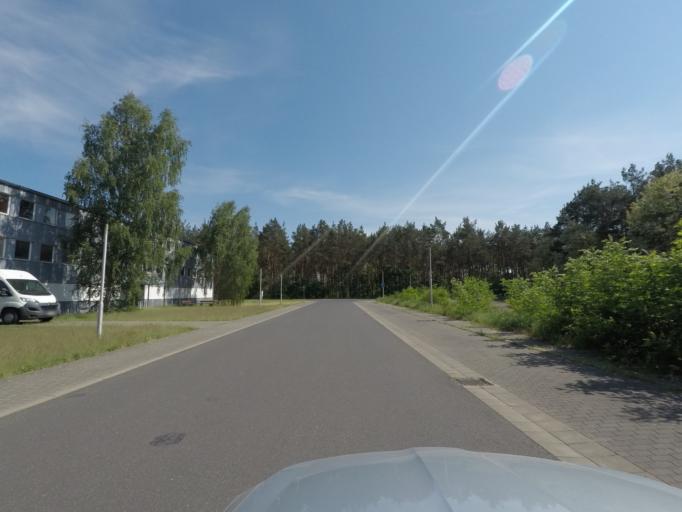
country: DE
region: Brandenburg
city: Britz
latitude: 52.8552
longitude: 13.7739
